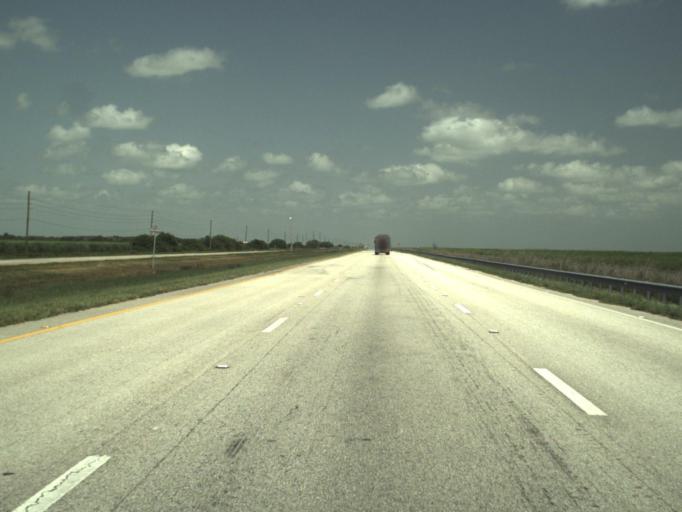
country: US
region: Florida
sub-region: Palm Beach County
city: Belle Glade Camp
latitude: 26.5124
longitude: -80.6751
